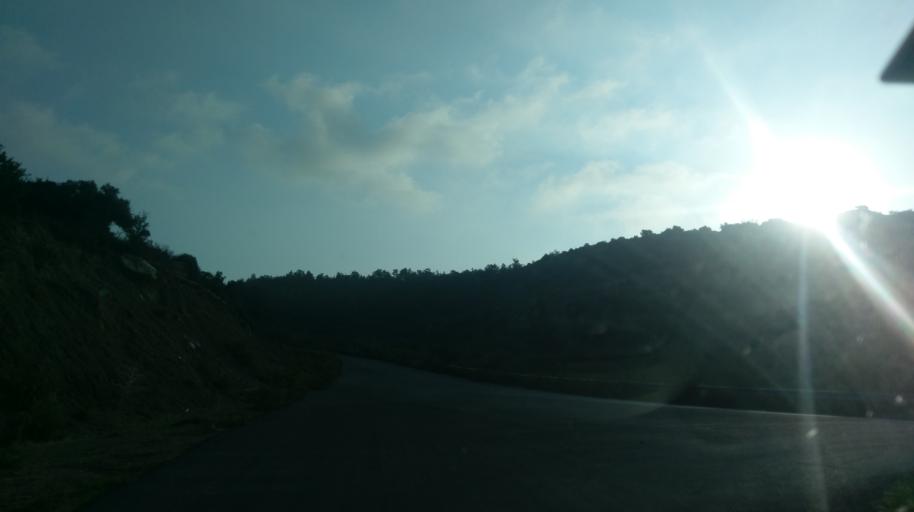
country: CY
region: Ammochostos
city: Trikomo
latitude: 35.4180
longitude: 33.9072
